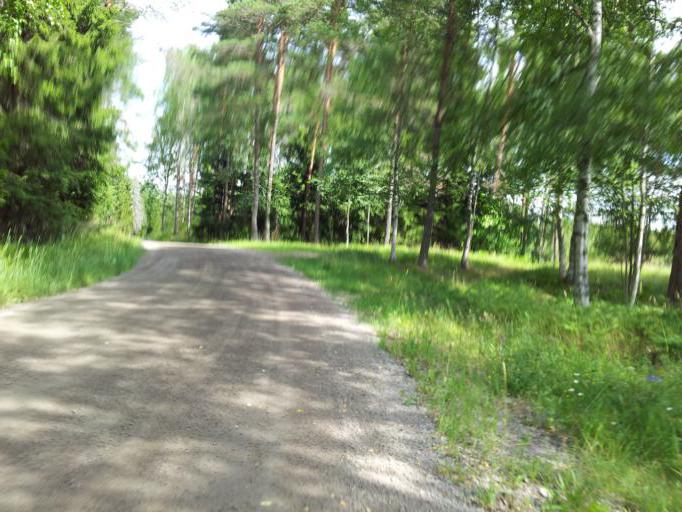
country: SE
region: Stockholm
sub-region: Norrtalje Kommun
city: Nykvarn
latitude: 59.8475
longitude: 18.2363
